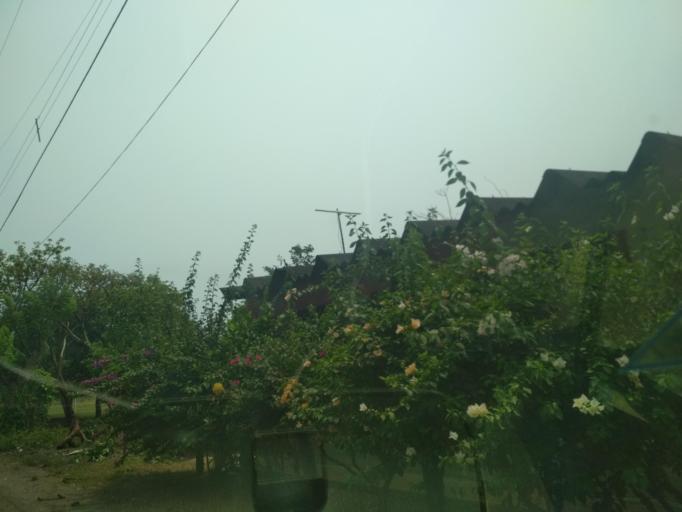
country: MX
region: Veracruz
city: El Tejar
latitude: 19.0672
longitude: -96.1538
